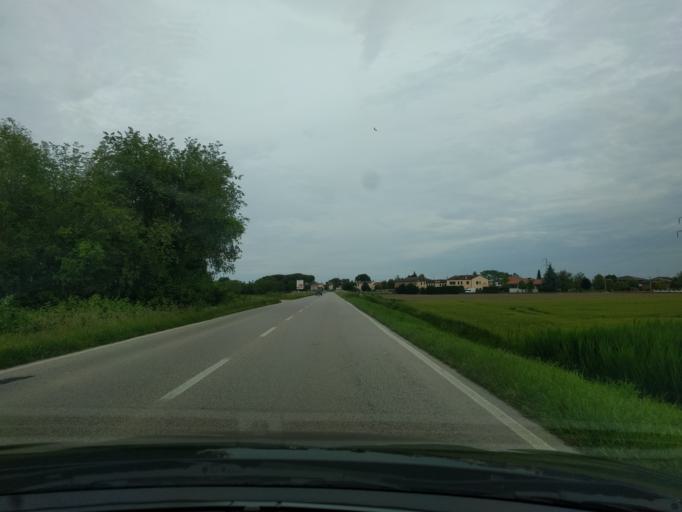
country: IT
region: Veneto
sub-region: Provincia di Rovigo
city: Sant'Apollinare
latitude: 45.0440
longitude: 11.8261
